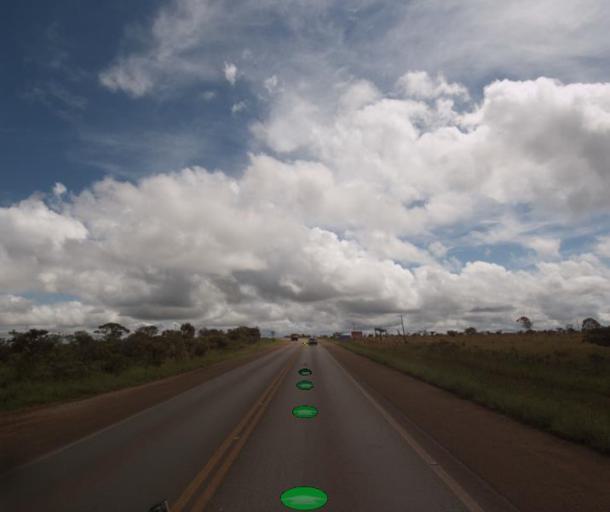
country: BR
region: Federal District
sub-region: Brasilia
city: Brasilia
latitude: -15.7392
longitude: -48.3867
